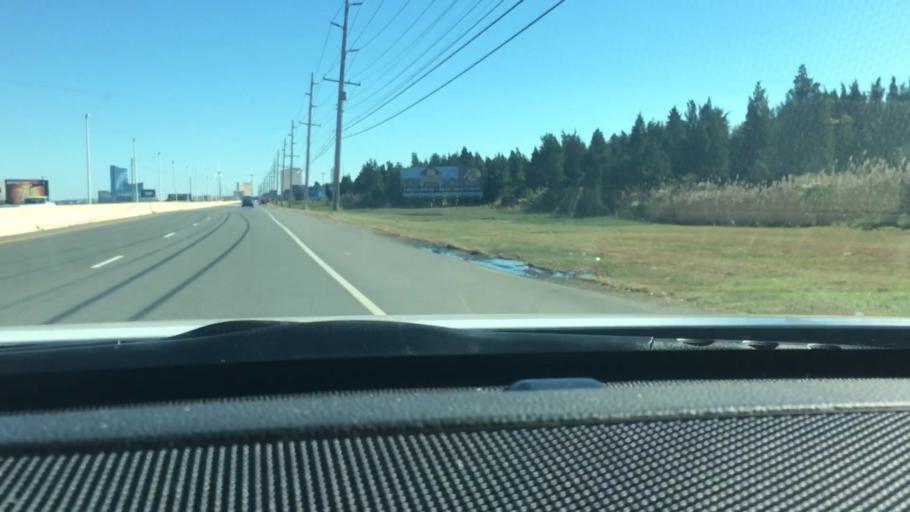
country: US
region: New Jersey
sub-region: Atlantic County
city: Absecon
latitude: 39.3885
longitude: -74.4785
